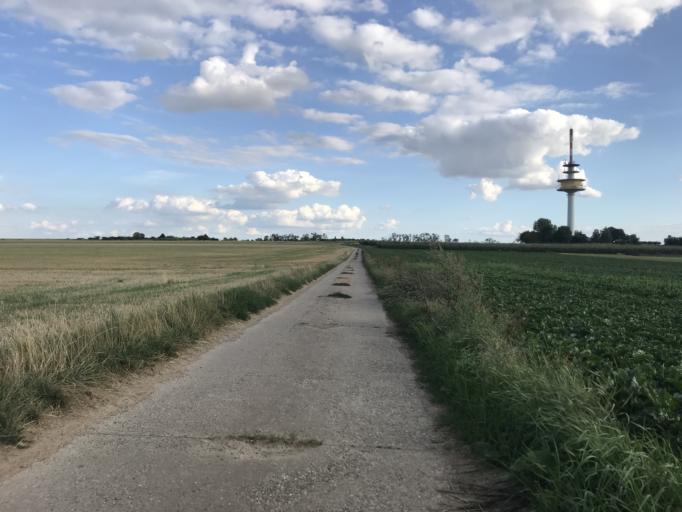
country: DE
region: Rheinland-Pfalz
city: Ober-Olm
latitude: 49.9472
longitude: 8.1724
